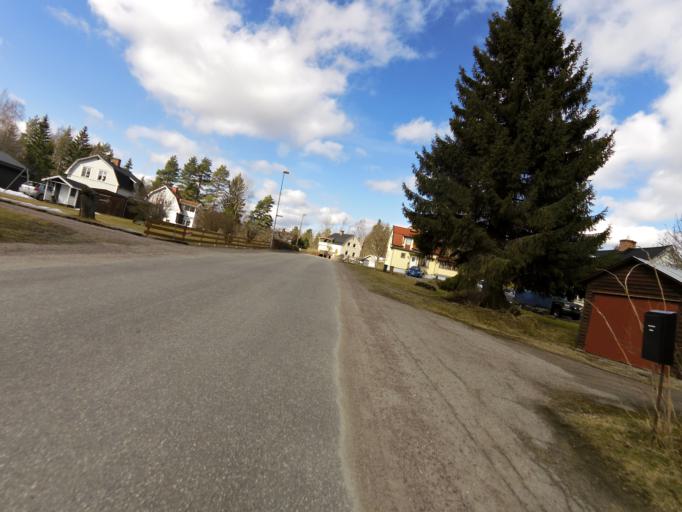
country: SE
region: Gaevleborg
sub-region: Hofors Kommun
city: Hofors
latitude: 60.5381
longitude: 16.2946
